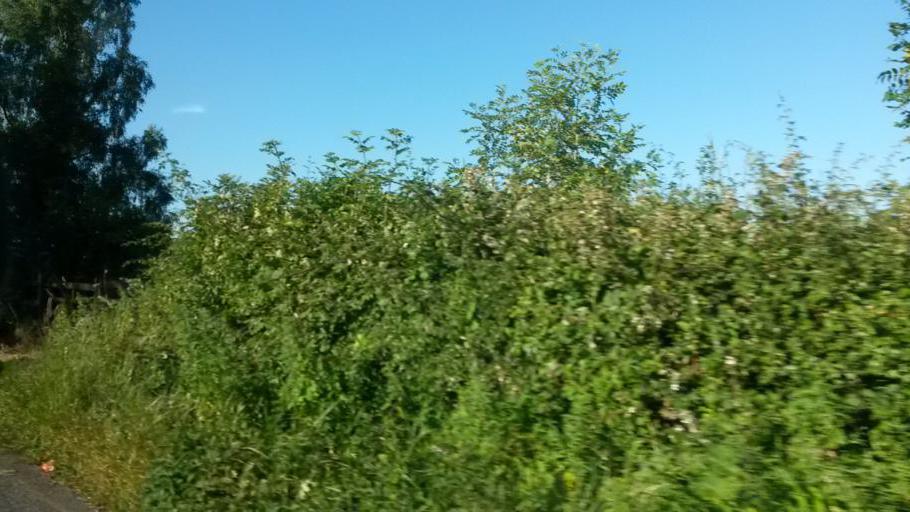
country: IE
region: Leinster
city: Ballymun
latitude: 53.4568
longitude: -6.2959
